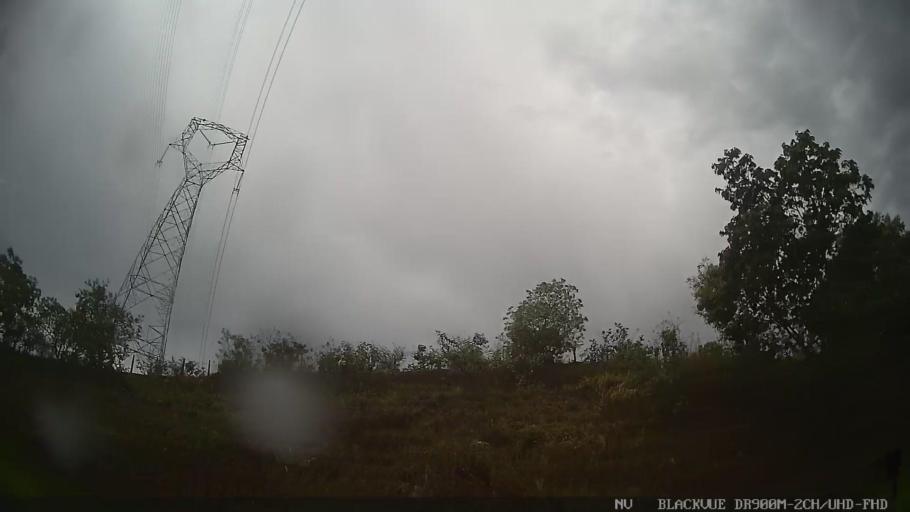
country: BR
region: Sao Paulo
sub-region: Pedreira
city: Pedreira
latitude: -22.7331
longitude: -46.9305
